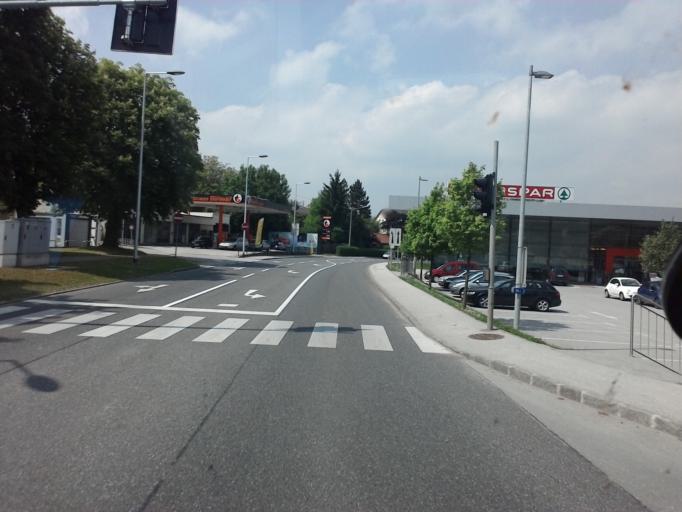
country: AT
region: Upper Austria
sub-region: Politischer Bezirk Steyr-Land
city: Bad Hall
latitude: 48.0382
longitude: 14.2088
